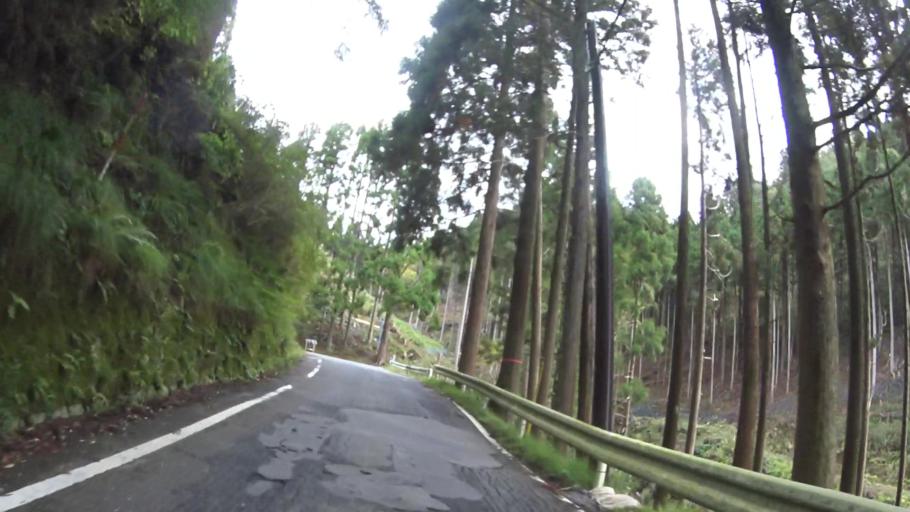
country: JP
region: Shiga Prefecture
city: Kitahama
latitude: 35.1576
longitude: 135.7876
